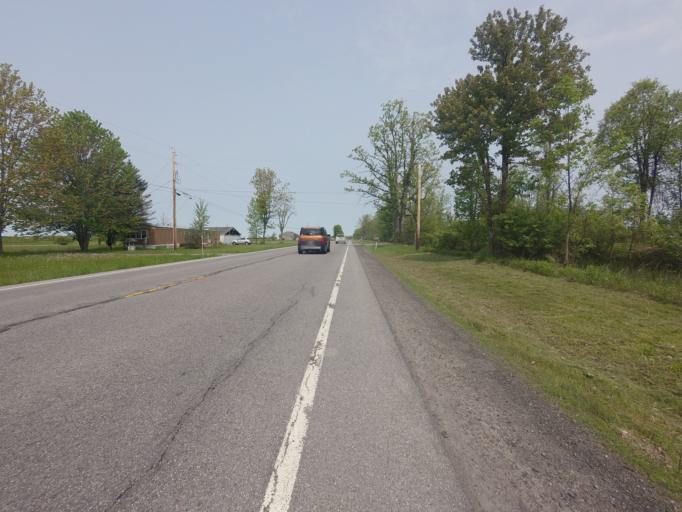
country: US
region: New York
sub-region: Jefferson County
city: Dexter
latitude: 44.0220
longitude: -76.0342
